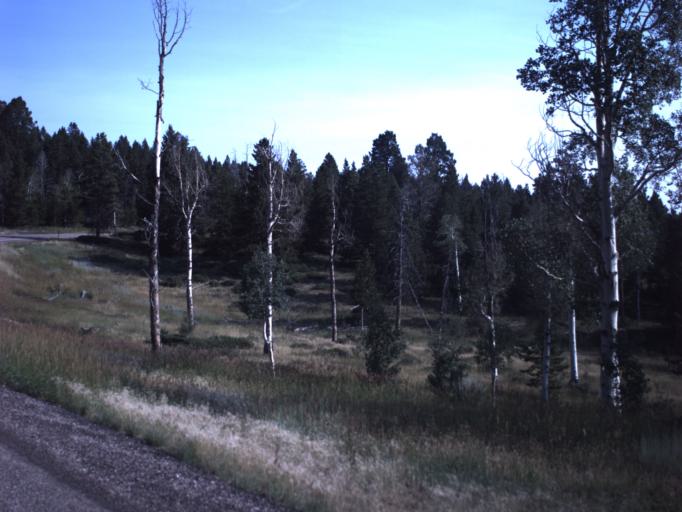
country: US
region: Utah
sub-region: Uintah County
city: Maeser
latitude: 40.7290
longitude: -109.4705
